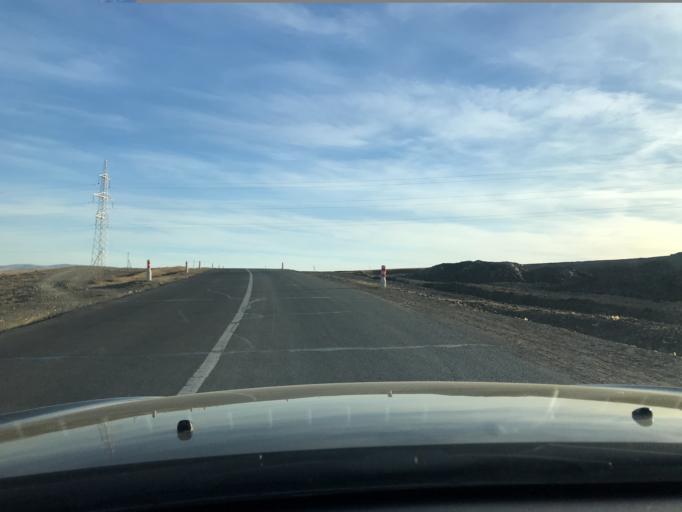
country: MN
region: Central Aimak
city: Dzuunmod
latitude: 47.7934
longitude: 107.3220
